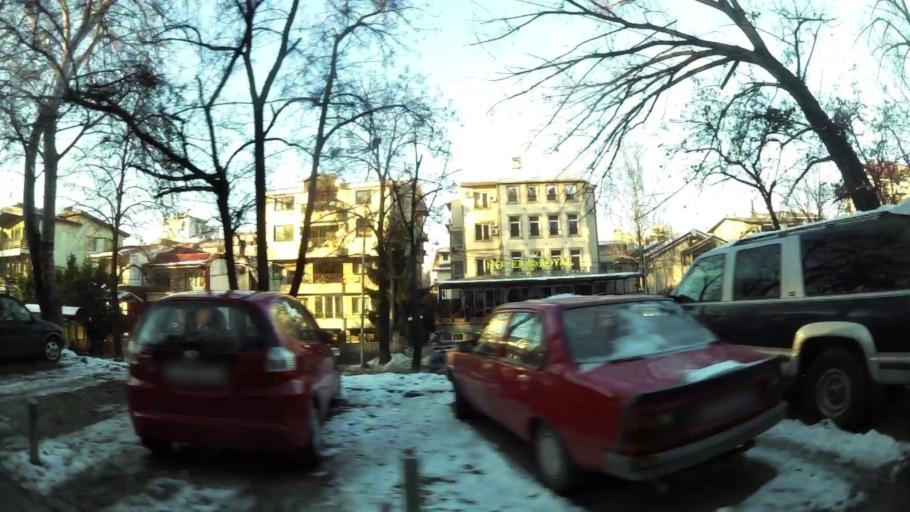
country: MK
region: Karpos
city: Skopje
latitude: 41.9935
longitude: 21.4088
